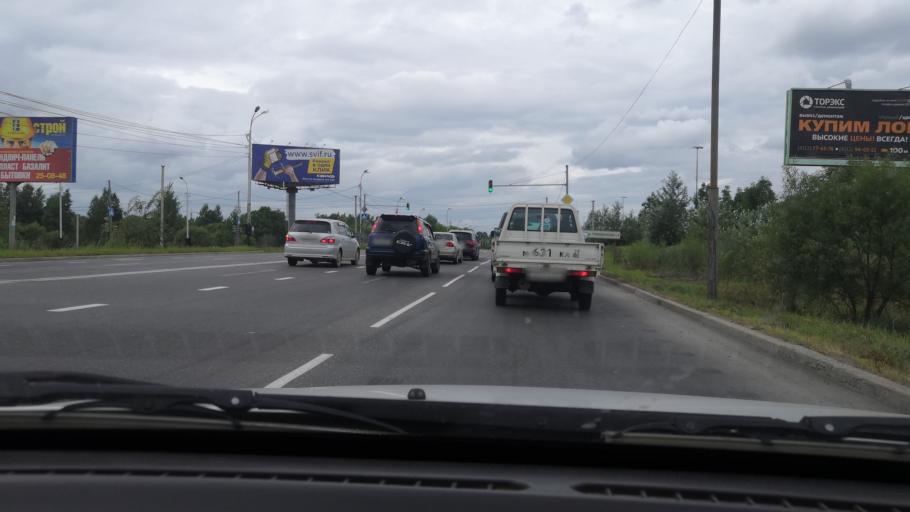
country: RU
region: Khabarovsk Krai
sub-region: Khabarovskiy Rayon
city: Khabarovsk
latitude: 48.5368
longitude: 135.0674
